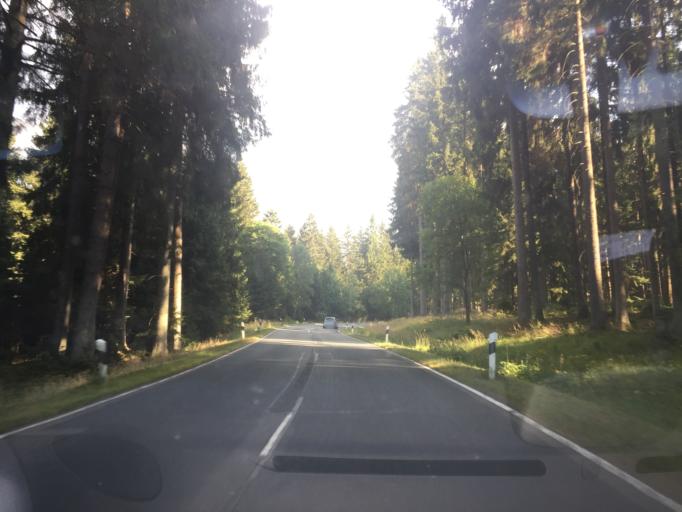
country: DE
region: Lower Saxony
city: Braunlage
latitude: 51.6958
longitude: 10.6255
